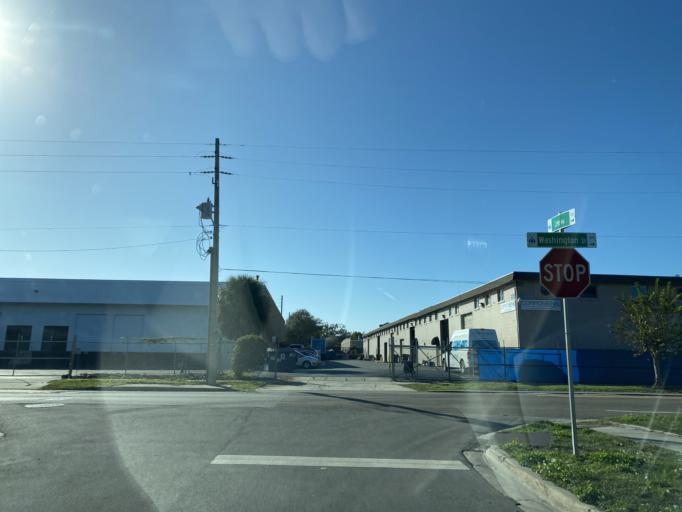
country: US
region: Florida
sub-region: Orange County
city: Orlando
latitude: 28.5441
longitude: -81.3912
